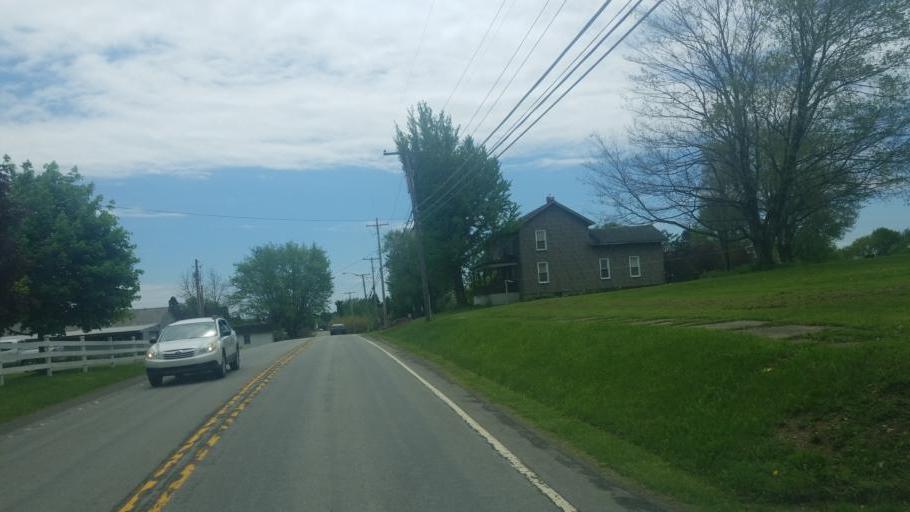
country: US
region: Pennsylvania
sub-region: Clarion County
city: Marianne
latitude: 41.2556
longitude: -79.4595
